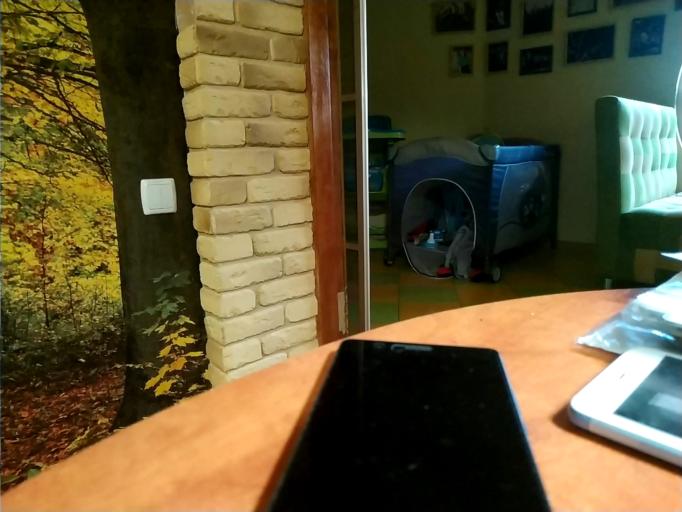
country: RU
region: Orjol
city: Znamenskoye
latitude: 53.5755
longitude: 35.4787
